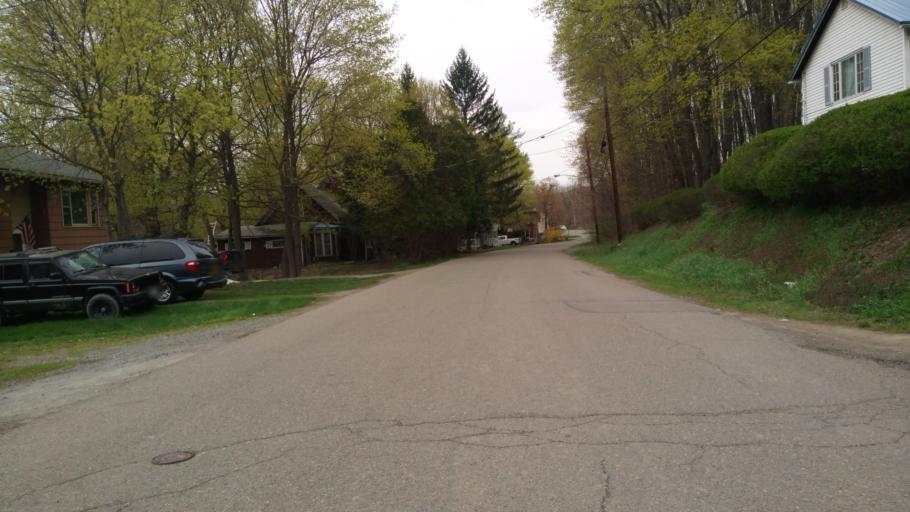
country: US
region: New York
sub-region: Chemung County
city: Southport
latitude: 42.0146
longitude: -76.7261
